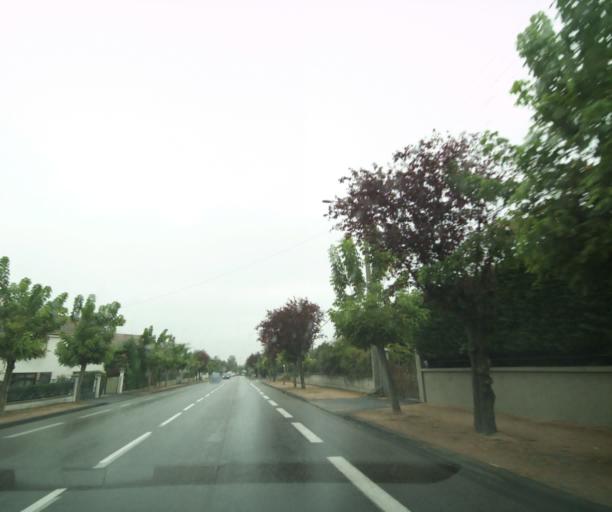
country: FR
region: Auvergne
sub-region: Departement du Puy-de-Dome
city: Cebazat
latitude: 45.8242
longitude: 3.1055
